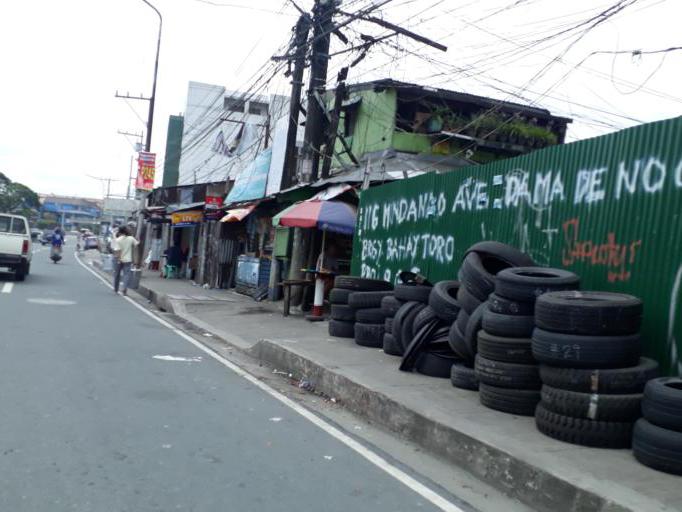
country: PH
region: Calabarzon
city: Bagong Pagasa
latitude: 14.6663
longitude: 121.0351
